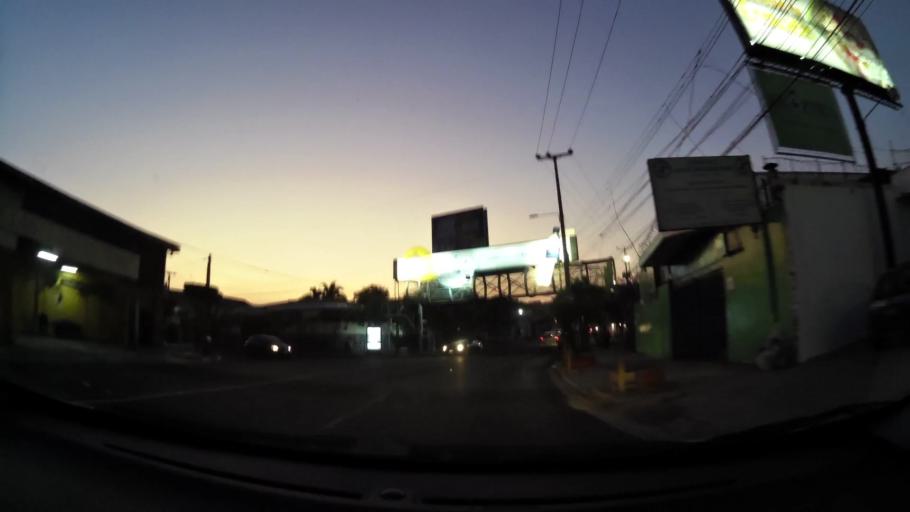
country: SV
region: La Libertad
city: Santa Tecla
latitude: 13.6781
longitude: -89.2675
